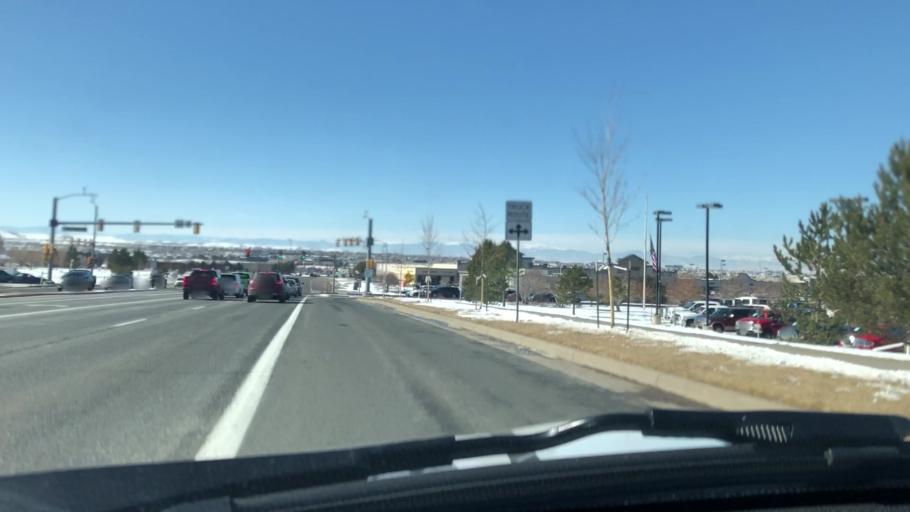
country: US
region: Colorado
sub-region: Douglas County
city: Parker
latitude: 39.5374
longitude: -104.7668
